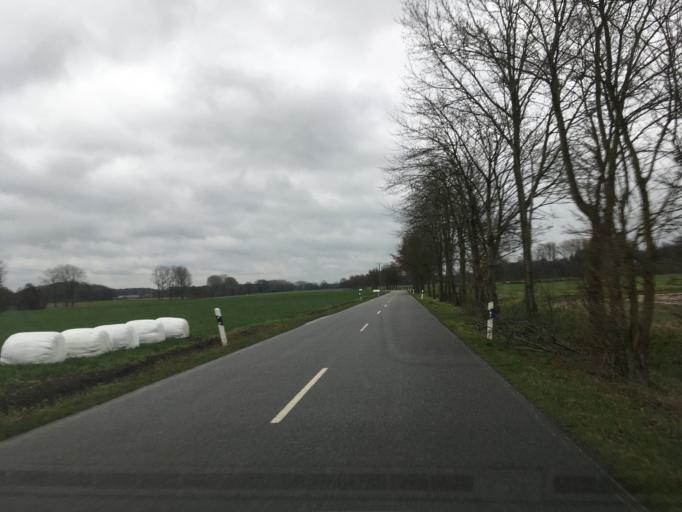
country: DE
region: North Rhine-Westphalia
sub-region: Regierungsbezirk Munster
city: Legden
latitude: 52.0507
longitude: 7.1468
